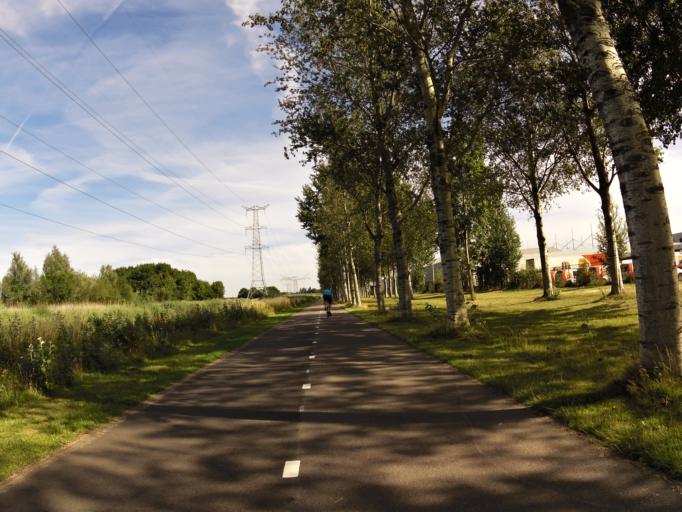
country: NL
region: North Brabant
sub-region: Gemeente Sint-Michielsgestel
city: Sint-Michielsgestel
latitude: 51.6893
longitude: 5.3605
